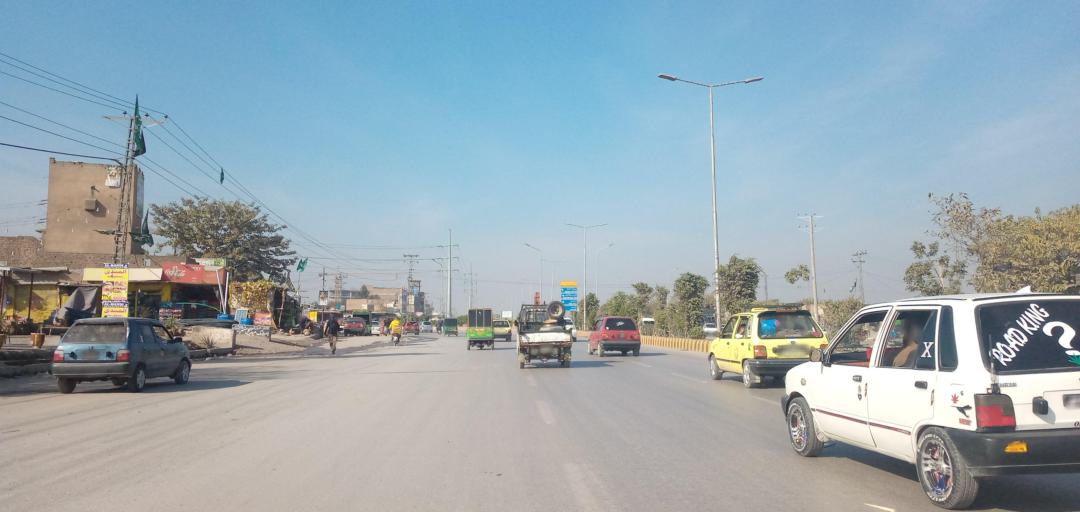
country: PK
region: Khyber Pakhtunkhwa
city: Peshawar
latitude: 33.9601
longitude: 71.5062
